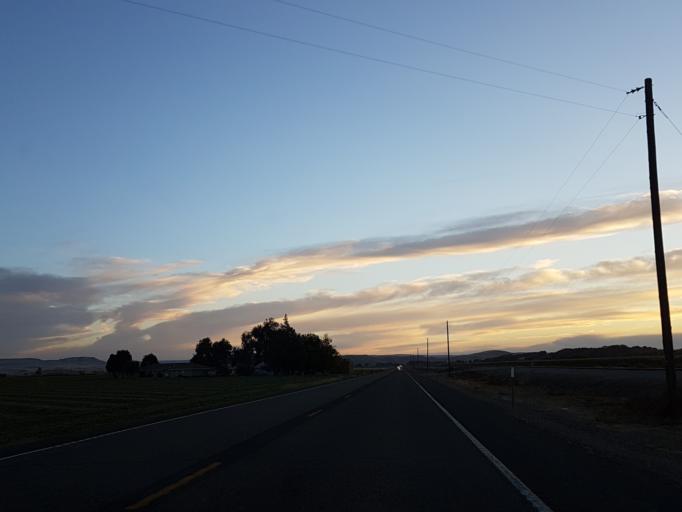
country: US
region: Oregon
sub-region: Malheur County
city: Vale
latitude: 43.9606
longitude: -117.2808
